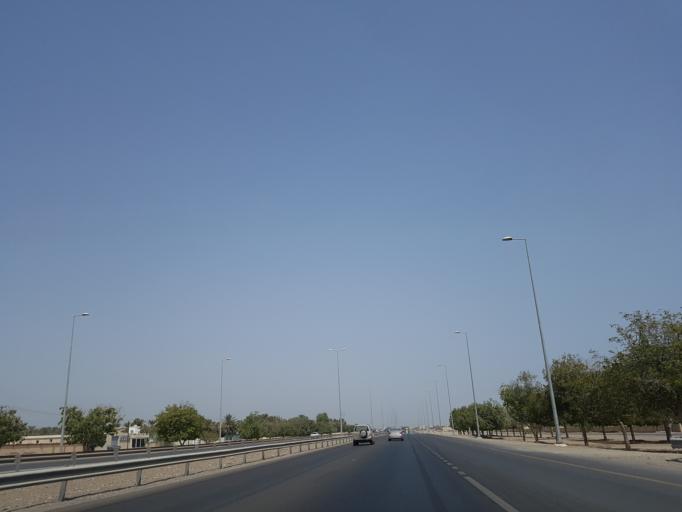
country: OM
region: Al Batinah
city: Saham
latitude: 24.0970
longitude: 56.9240
